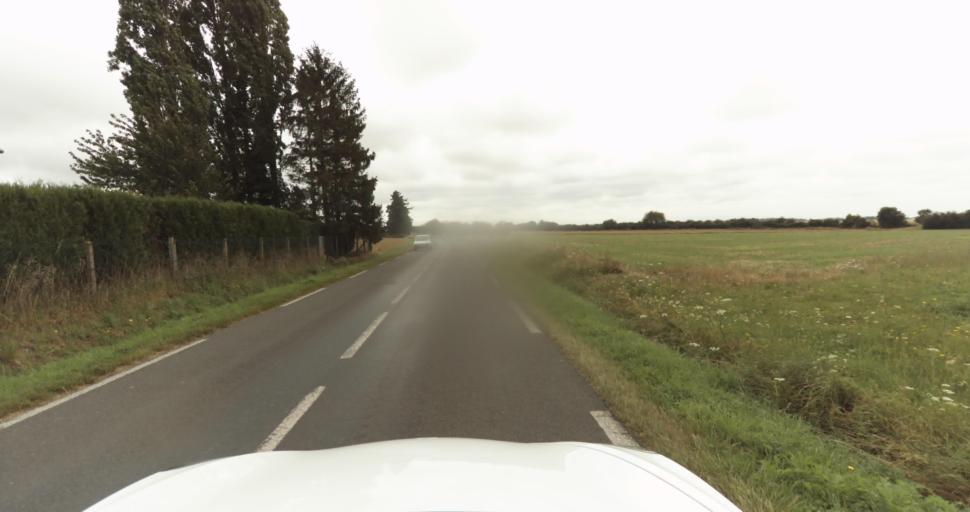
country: FR
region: Haute-Normandie
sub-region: Departement de l'Eure
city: Claville
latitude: 49.0699
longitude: 1.0675
